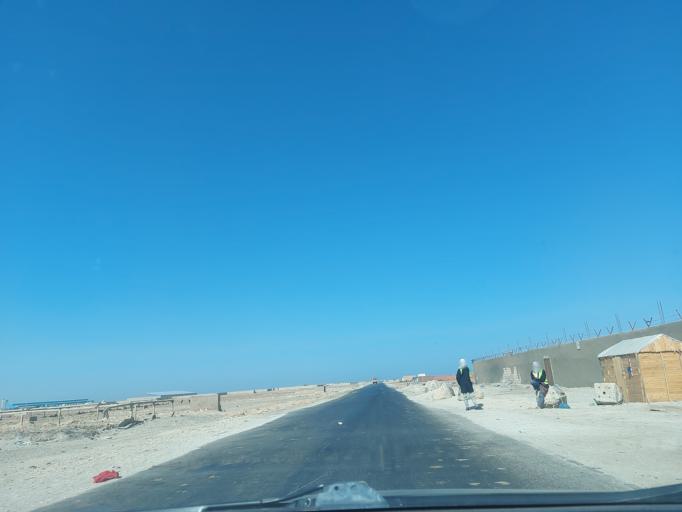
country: MR
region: Nouakchott
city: Nouakchott
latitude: 18.0584
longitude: -16.0129
